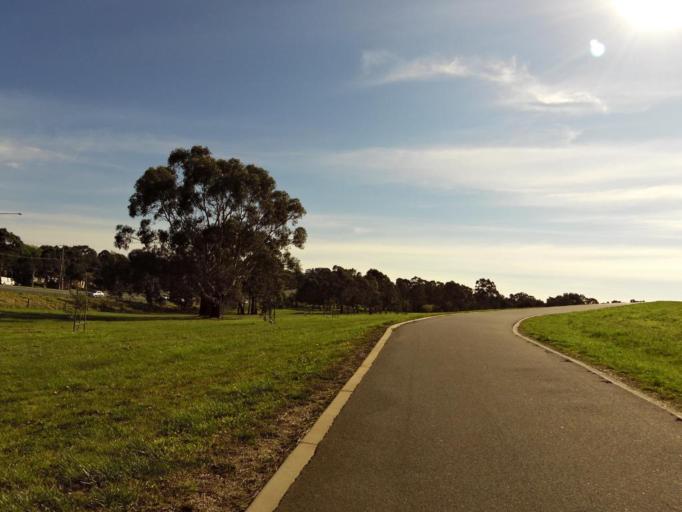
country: AU
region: Victoria
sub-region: Monash
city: Mulgrave
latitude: -37.9079
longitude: 145.2036
